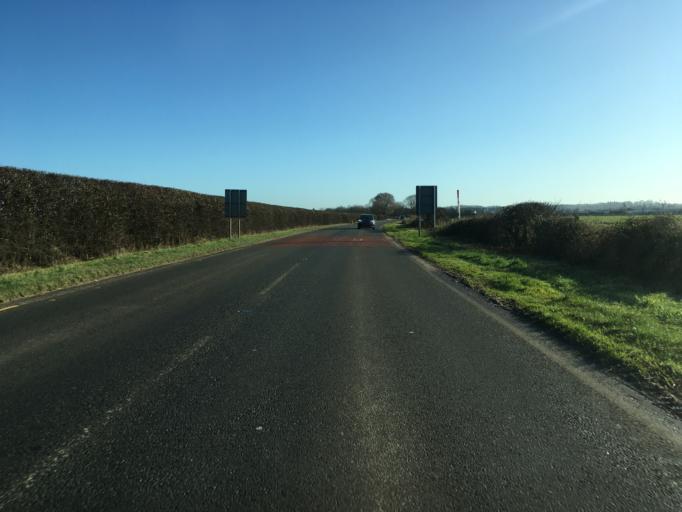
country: GB
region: England
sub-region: Warwickshire
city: Wellesbourne Mountford
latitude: 52.1982
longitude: -1.6154
